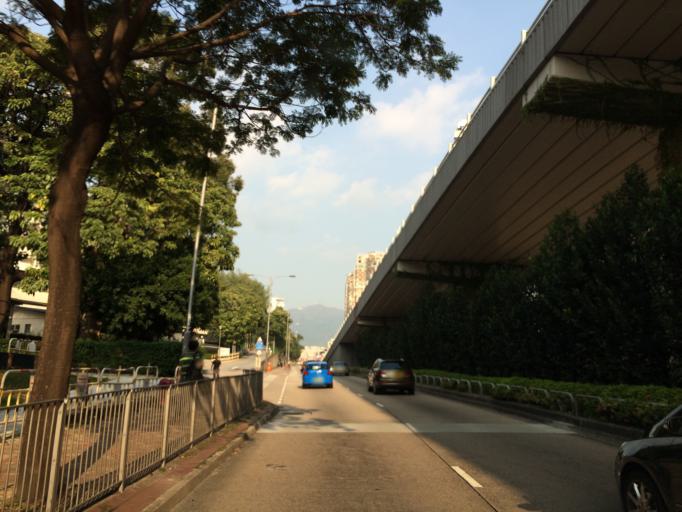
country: HK
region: Kowloon City
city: Kowloon
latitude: 22.3218
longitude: 114.1784
